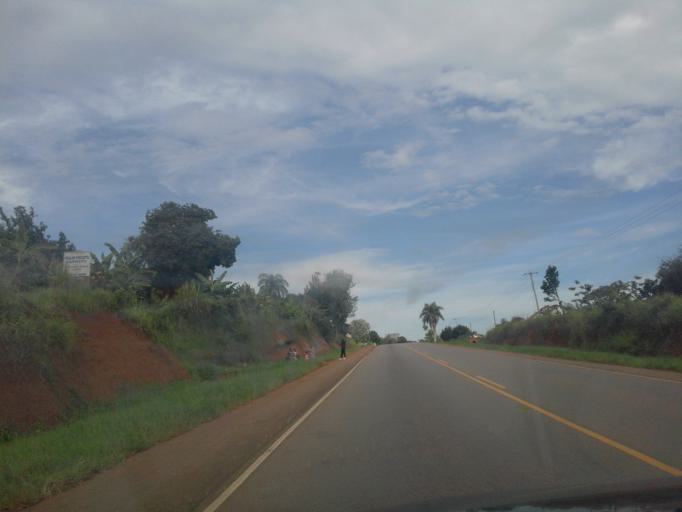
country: UG
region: Central Region
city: Masaka
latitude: -0.3459
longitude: 31.6175
